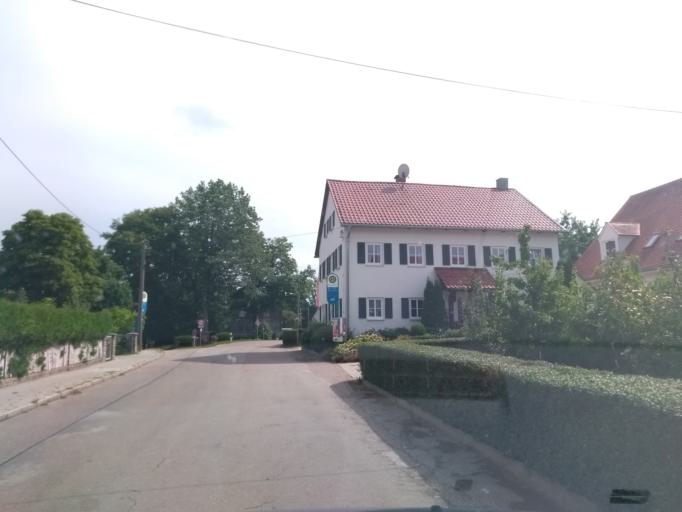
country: DE
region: Bavaria
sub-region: Upper Bavaria
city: Schwabhausen
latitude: 48.3828
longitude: 11.3490
